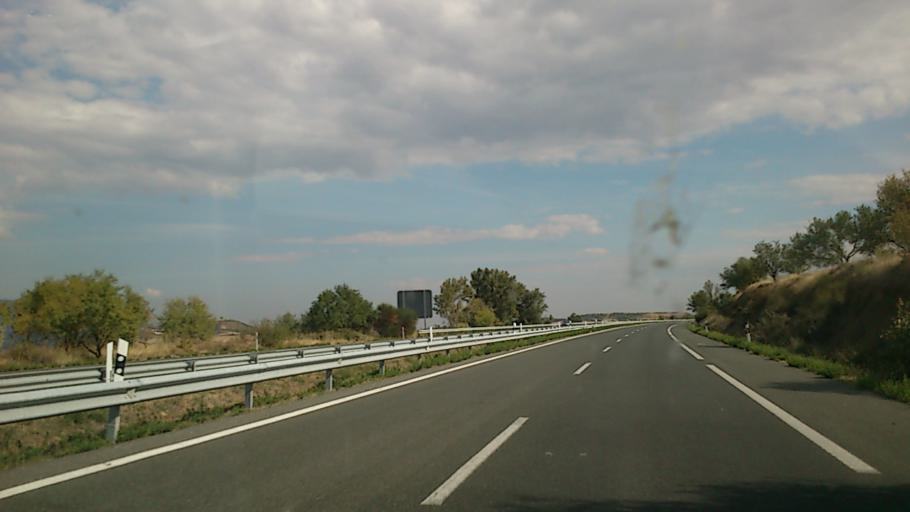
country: ES
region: La Rioja
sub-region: Provincia de La Rioja
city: Ollauri
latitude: 42.5511
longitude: -2.8558
